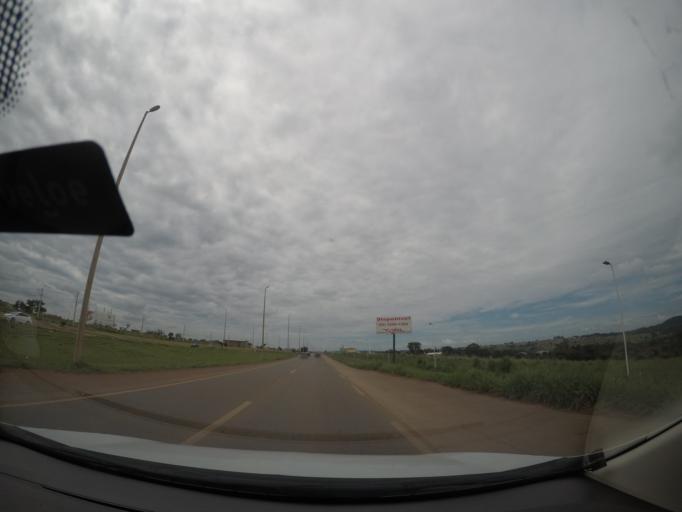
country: BR
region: Goias
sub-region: Goianira
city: Goianira
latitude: -16.5289
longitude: -49.4102
